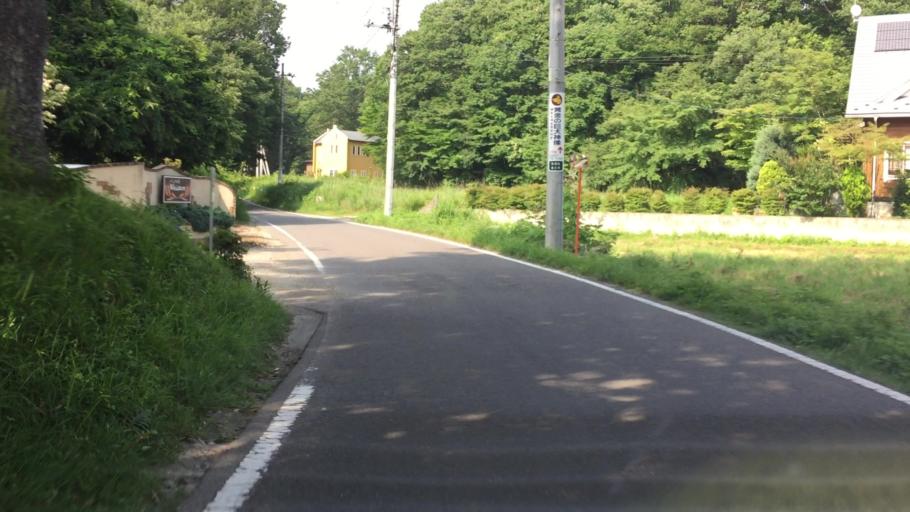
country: JP
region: Tochigi
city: Kuroiso
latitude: 37.0315
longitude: 140.0231
